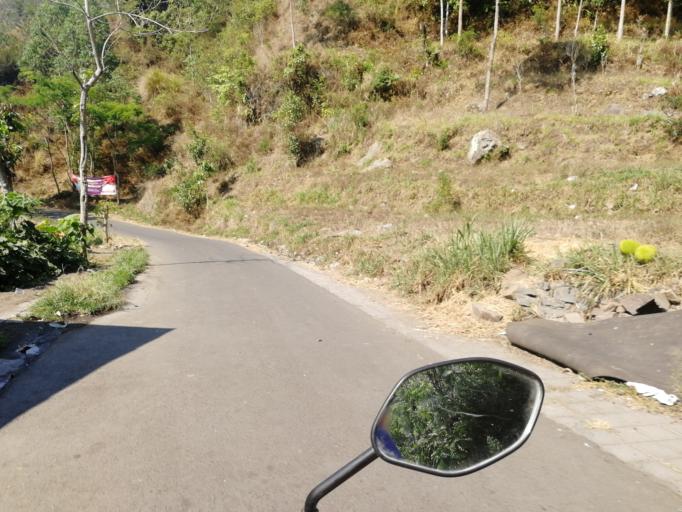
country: ID
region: Bali
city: Banjar Trunyan
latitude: -8.2532
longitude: 115.4267
